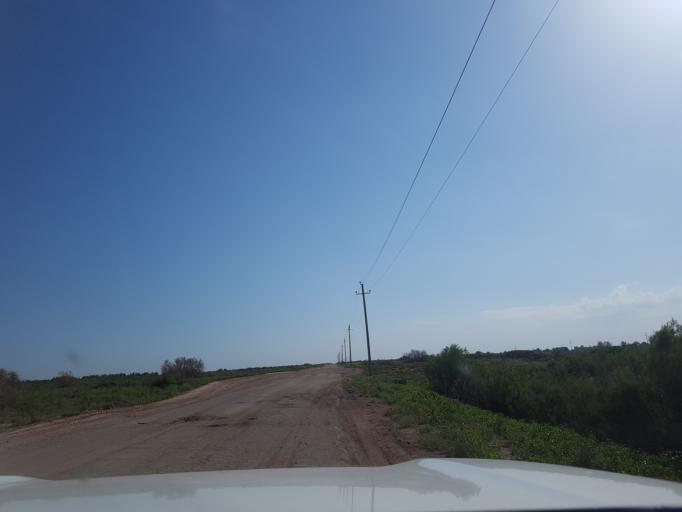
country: TM
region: Dasoguz
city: Koeneuergench
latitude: 42.0518
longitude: 58.8323
